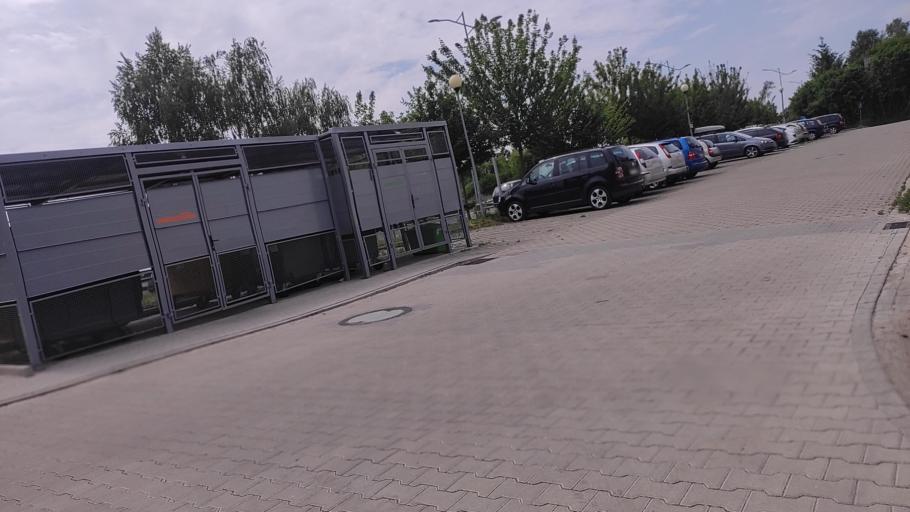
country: PL
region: Greater Poland Voivodeship
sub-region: Powiat poznanski
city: Swarzedz
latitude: 52.3962
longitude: 17.0810
